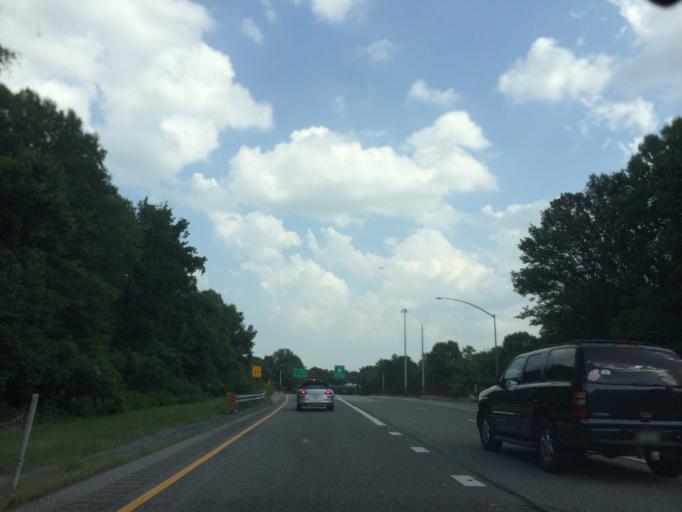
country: US
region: Maryland
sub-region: Howard County
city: Savage
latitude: 39.1598
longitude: -76.8307
